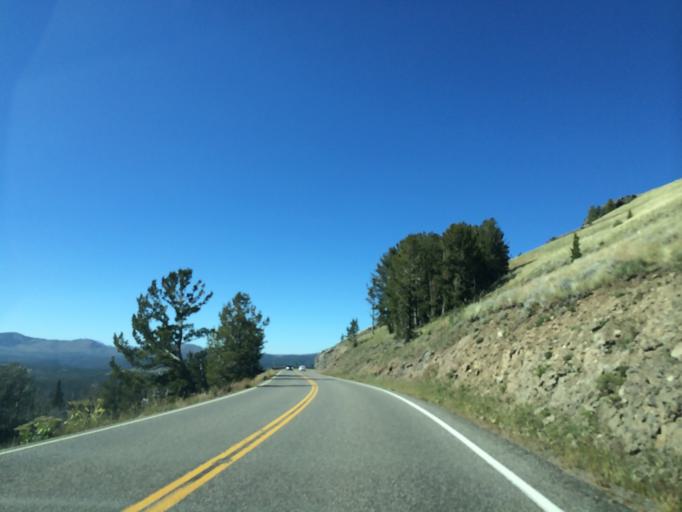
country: US
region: Montana
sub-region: Gallatin County
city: West Yellowstone
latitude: 44.8018
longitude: -110.4460
